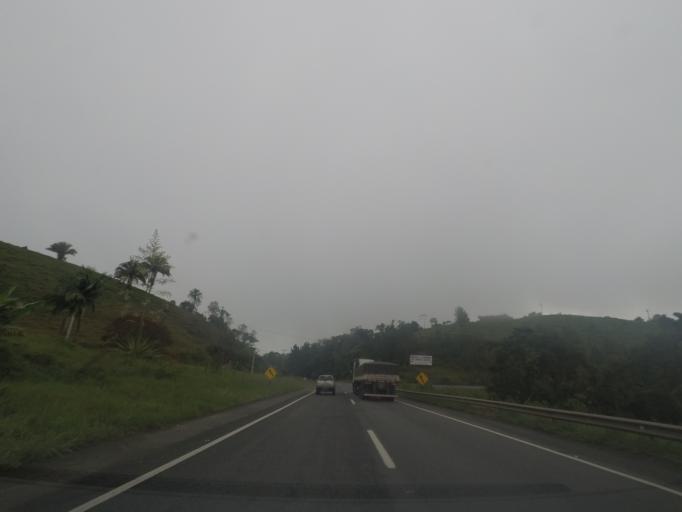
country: BR
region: Parana
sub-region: Antonina
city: Antonina
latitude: -25.0434
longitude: -48.5535
